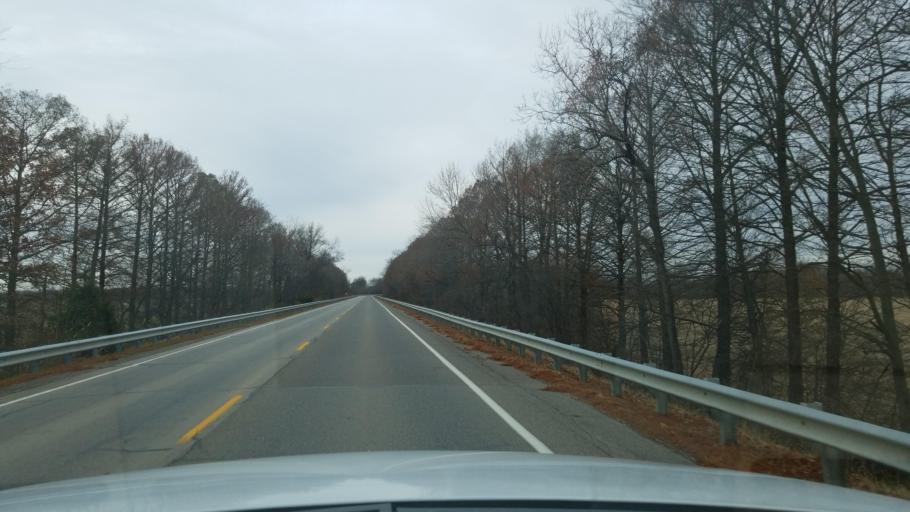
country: US
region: Indiana
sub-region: Posey County
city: Mount Vernon
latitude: 37.9290
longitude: -87.9908
